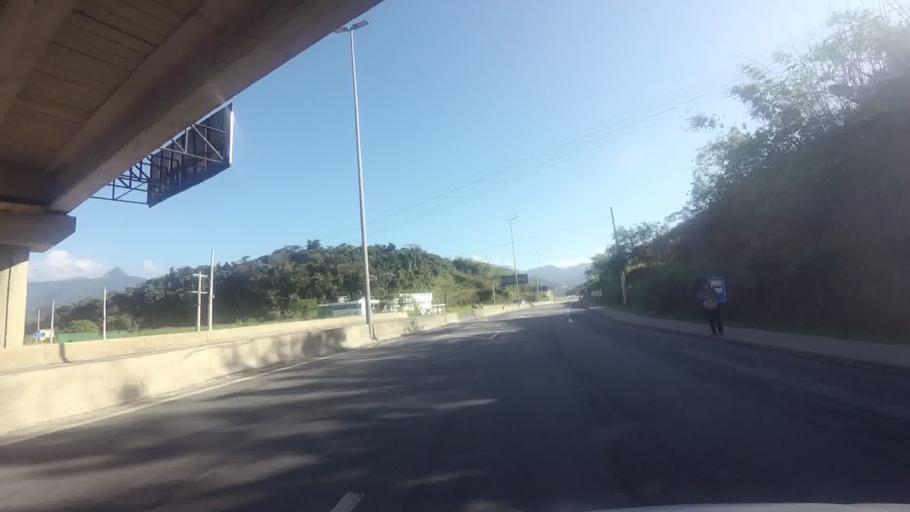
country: BR
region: Rio de Janeiro
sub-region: Petropolis
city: Petropolis
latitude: -22.6077
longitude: -43.2859
